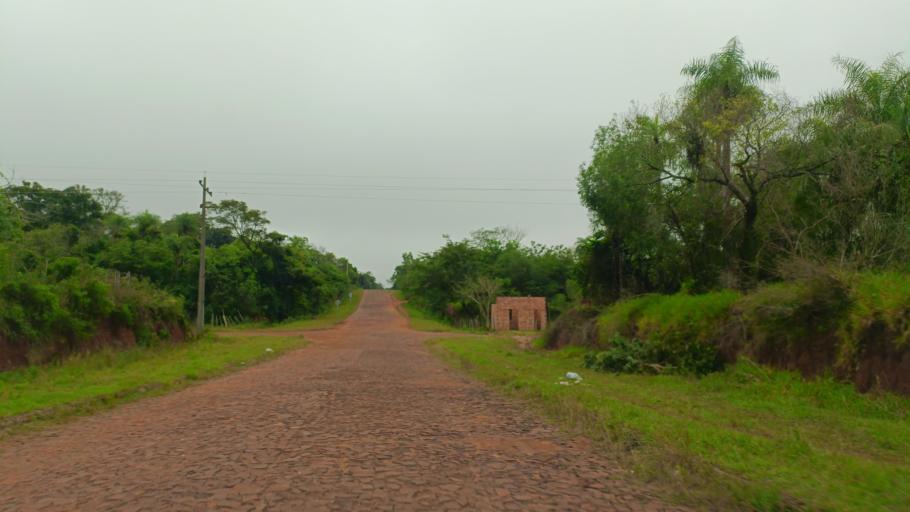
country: PY
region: Misiones
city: Santa Maria
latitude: -26.8729
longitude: -57.0120
